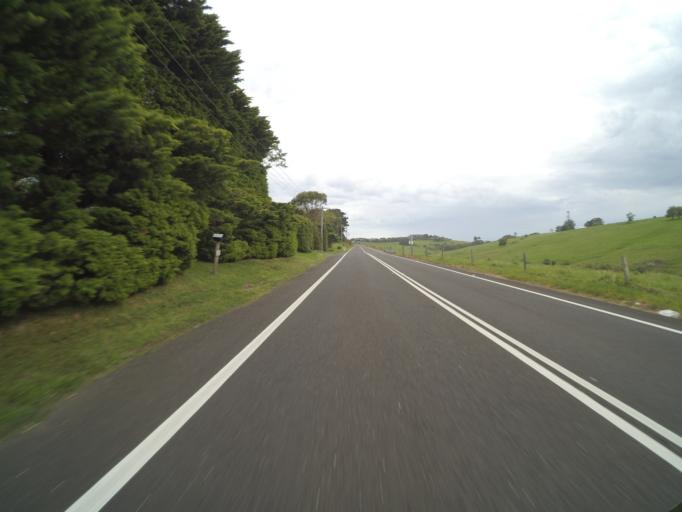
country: AU
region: New South Wales
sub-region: Kiama
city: Kiama
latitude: -34.6623
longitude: 150.8283
